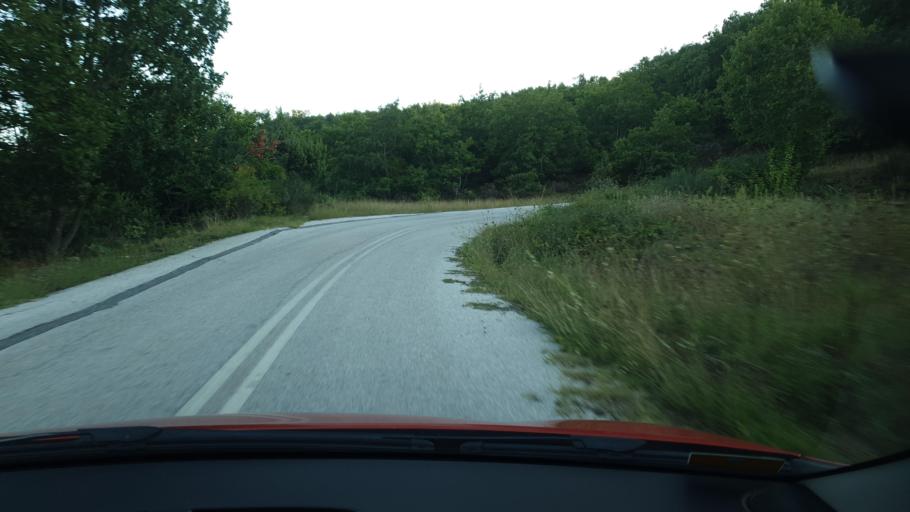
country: GR
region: Central Macedonia
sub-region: Nomos Chalkidikis
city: Galatista
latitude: 40.5169
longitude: 23.2715
